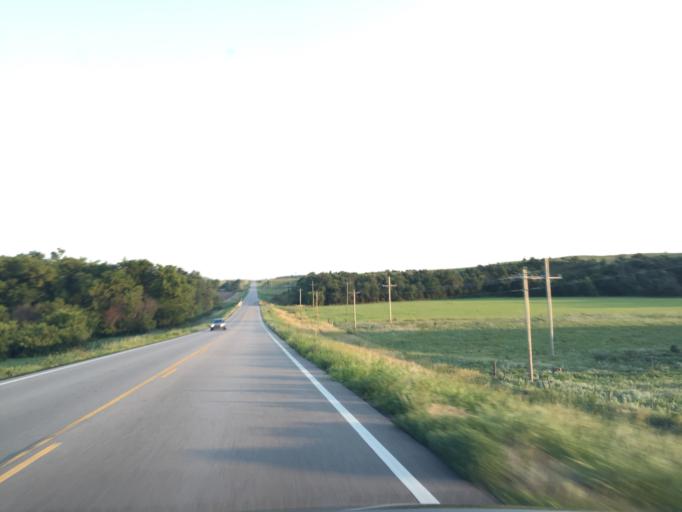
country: US
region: Kansas
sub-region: Ellsworth County
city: Ellsworth
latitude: 38.6254
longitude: -98.2019
